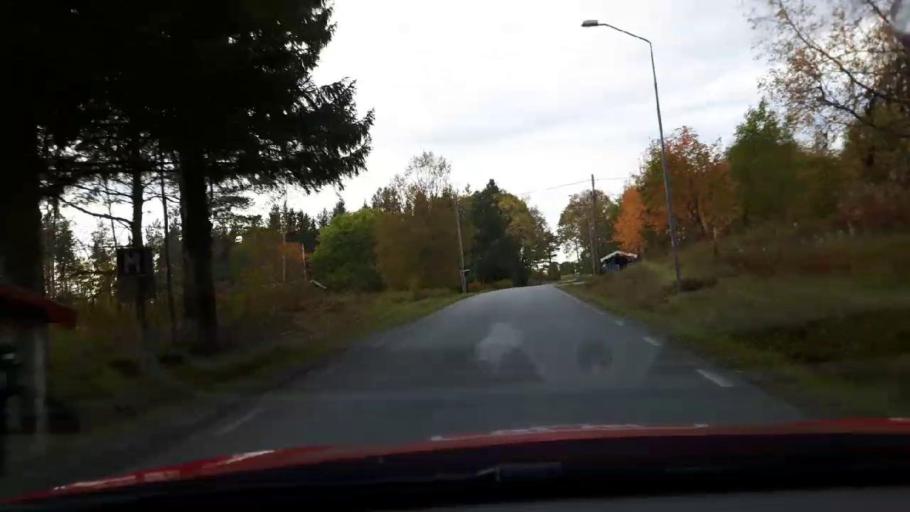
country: SE
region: Jaemtland
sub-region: Krokoms Kommun
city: Krokom
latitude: 63.3637
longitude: 14.4965
